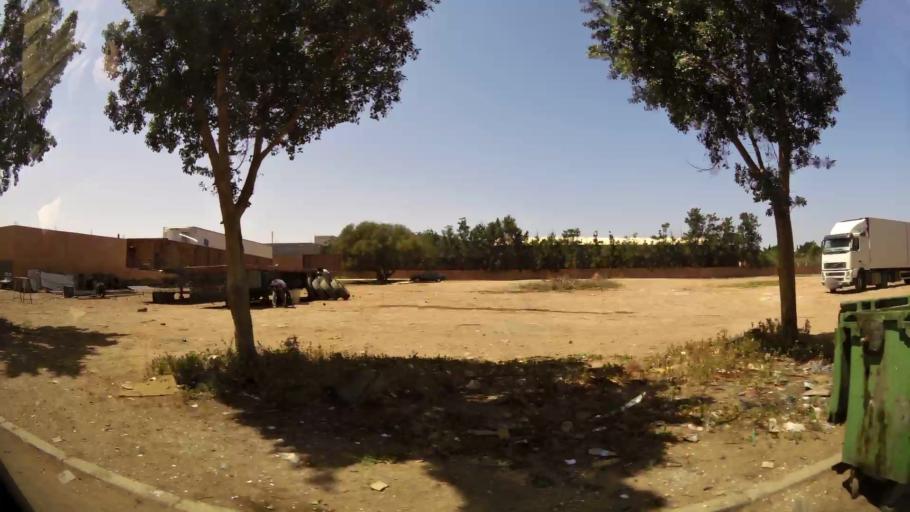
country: MA
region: Souss-Massa-Draa
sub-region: Inezgane-Ait Mellou
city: Inezgane
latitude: 30.3362
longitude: -9.4828
